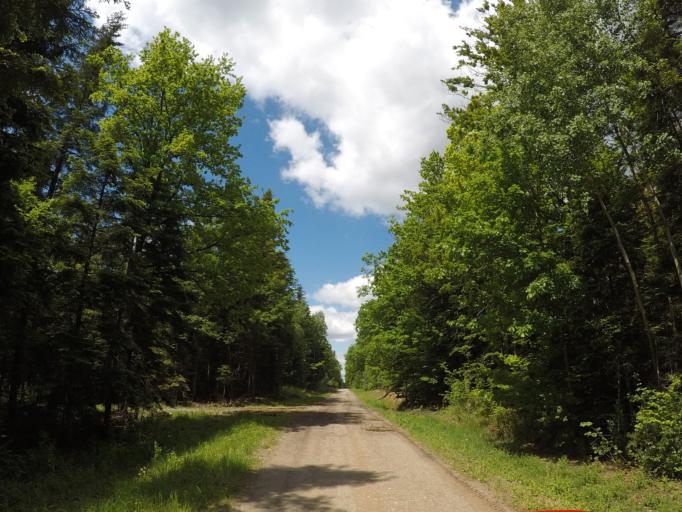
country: PL
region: Swietokrzyskie
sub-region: Powiat kielecki
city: Domaszowice
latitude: 50.9130
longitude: 20.6534
